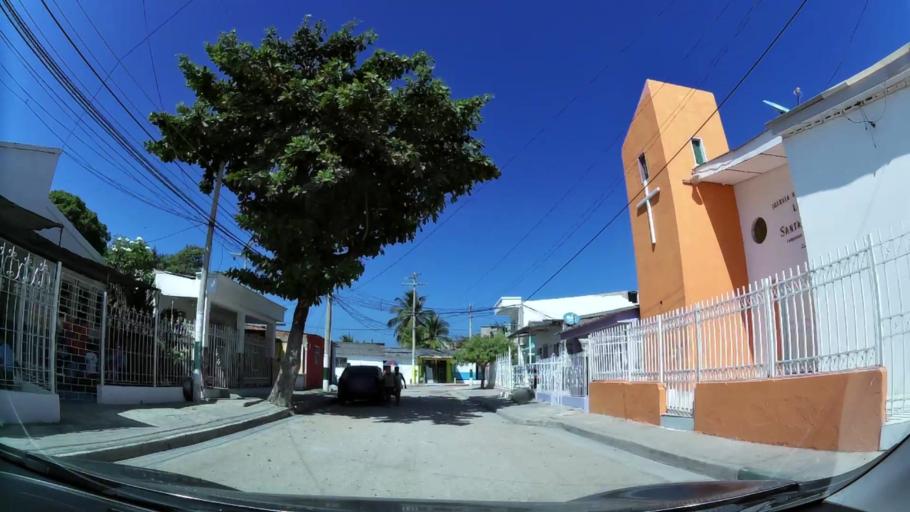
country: CO
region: Bolivar
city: Cartagena
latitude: 10.4395
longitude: -75.5157
